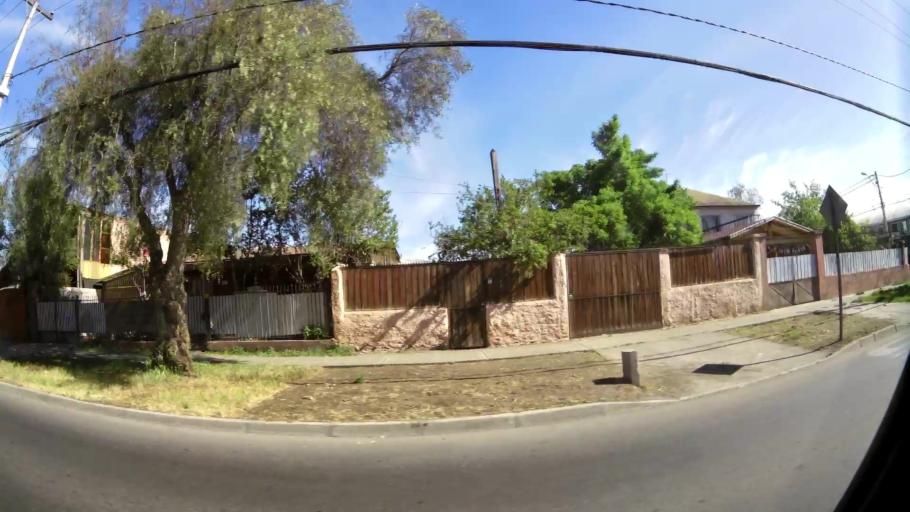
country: CL
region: Santiago Metropolitan
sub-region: Provincia de Santiago
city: Lo Prado
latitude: -33.4896
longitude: -70.7140
